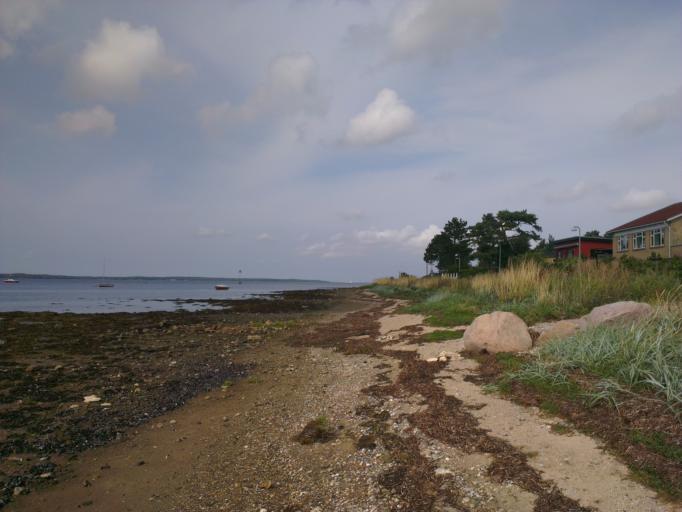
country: DK
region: Capital Region
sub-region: Frederikssund Kommune
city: Frederikssund
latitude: 55.8481
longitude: 12.0444
